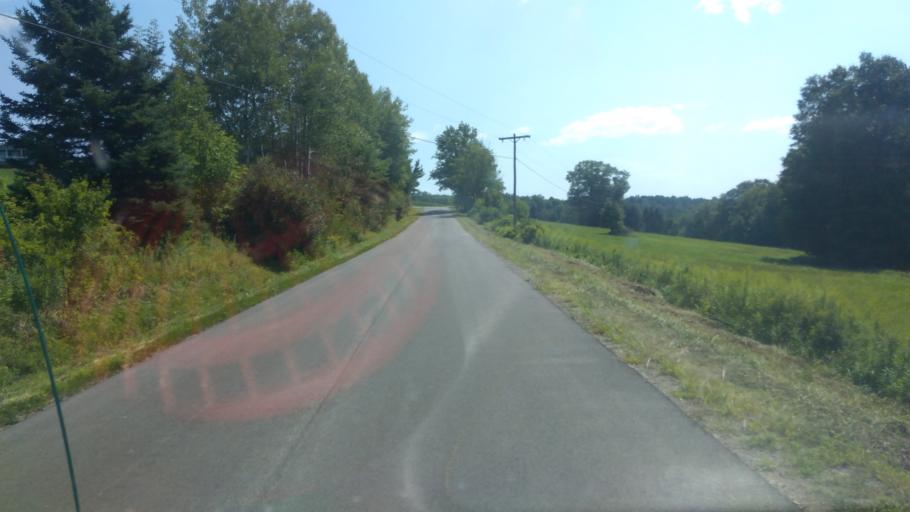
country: US
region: New York
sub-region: Steuben County
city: Canisteo
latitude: 42.3582
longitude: -77.5500
